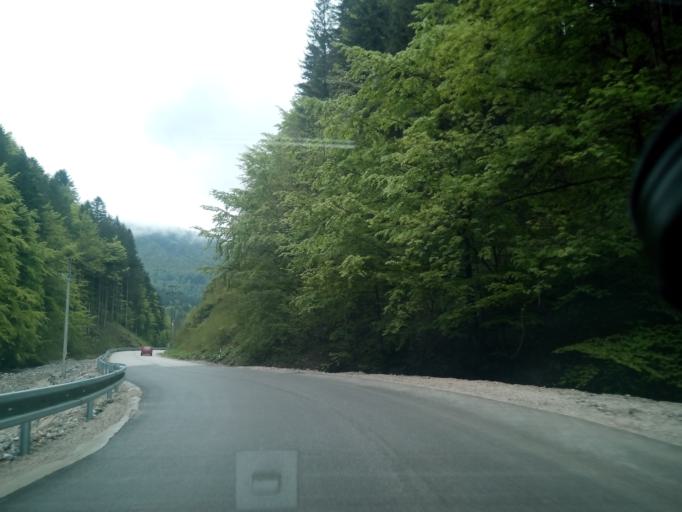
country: SK
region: Zilinsky
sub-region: Okres Zilina
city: Terchova
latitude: 49.2142
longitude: 19.0375
